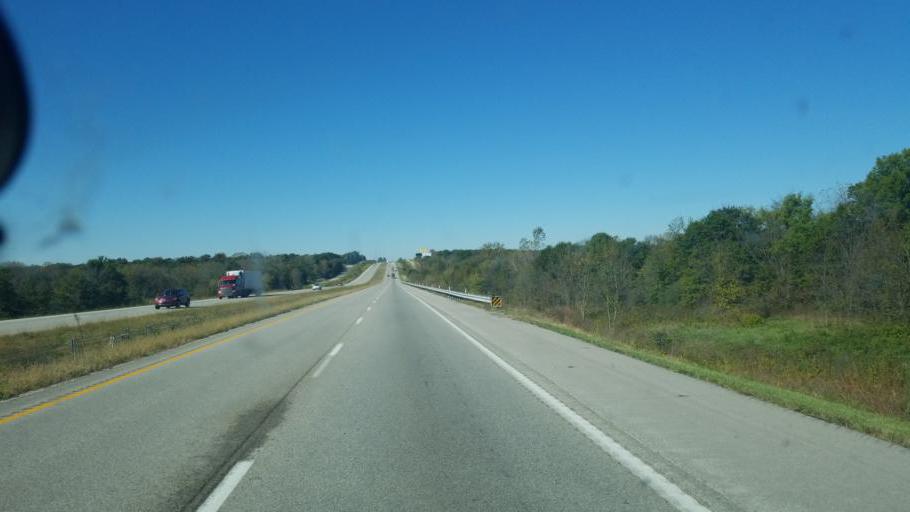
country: US
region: Missouri
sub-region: Saline County
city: Sweet Springs
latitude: 38.9745
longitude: -93.3580
